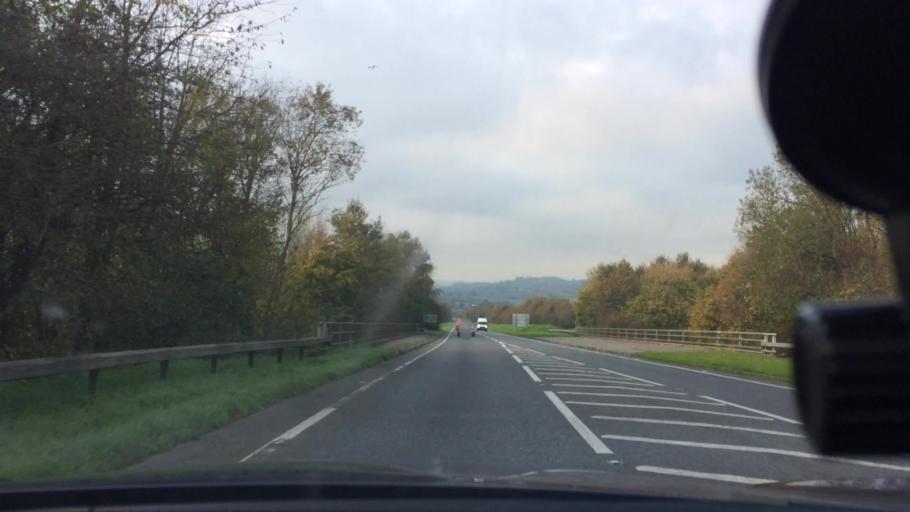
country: GB
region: England
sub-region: Devon
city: Axminster
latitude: 50.7701
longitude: -3.0044
